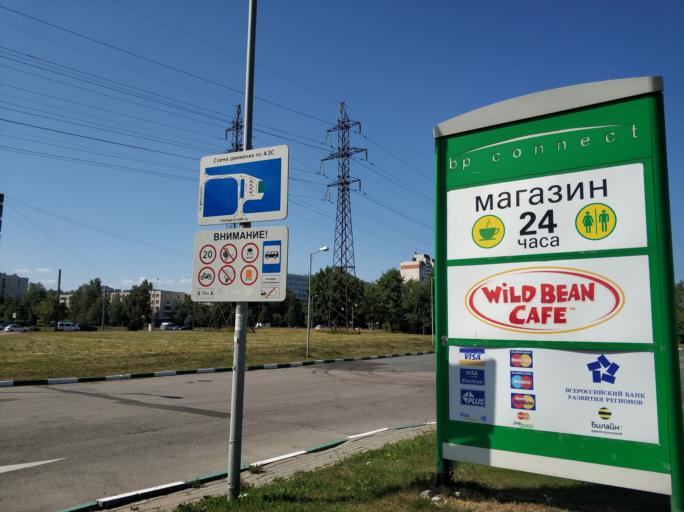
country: RU
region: St.-Petersburg
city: Grazhdanka
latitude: 60.0231
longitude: 30.4073
